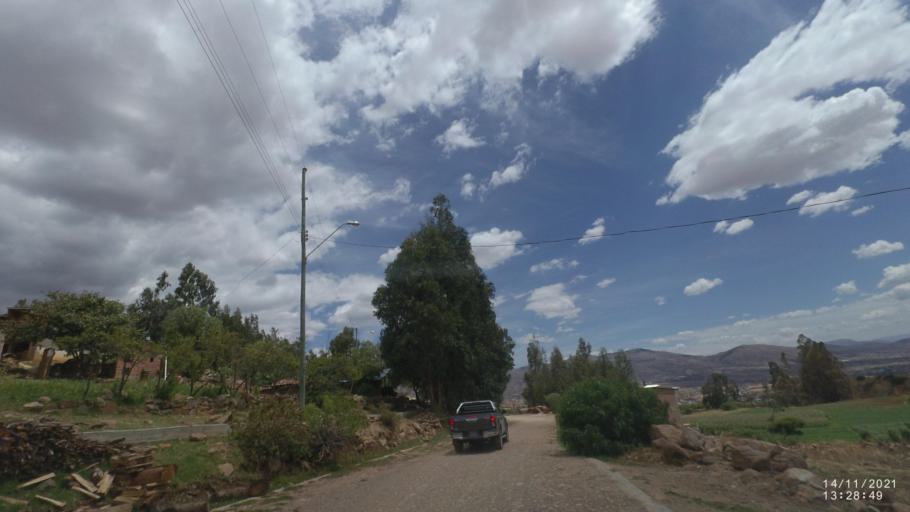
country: BO
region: Cochabamba
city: Colomi
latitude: -17.3864
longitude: -65.9852
